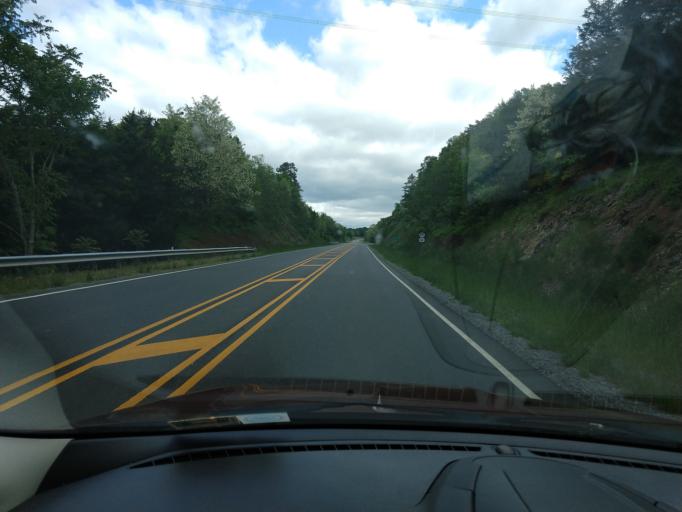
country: US
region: Virginia
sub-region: Wythe County
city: Wytheville
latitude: 36.8707
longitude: -80.9835
